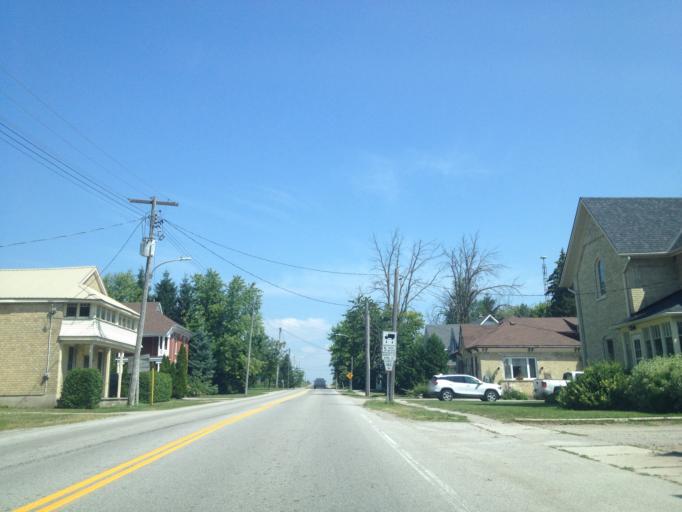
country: CA
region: Ontario
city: Huron East
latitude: 43.3900
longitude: -81.2219
